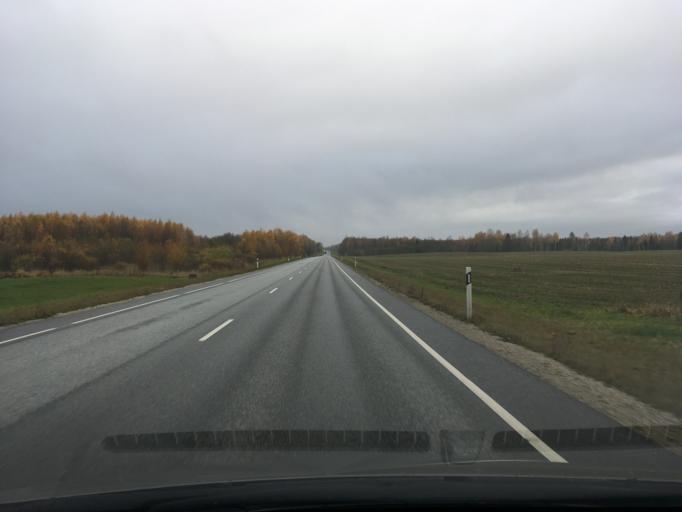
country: EE
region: Tartu
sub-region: Noo vald
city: Noo
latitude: 58.2904
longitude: 26.5655
